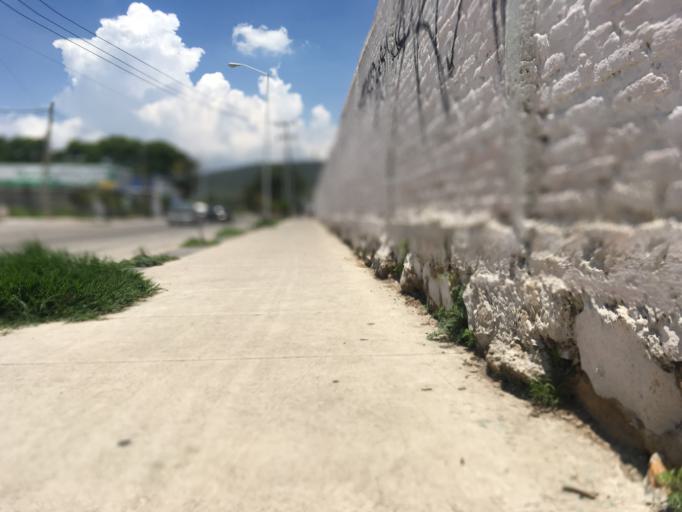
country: MX
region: Jalisco
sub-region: Tlajomulco de Zuniga
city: Jardines de San Sebastian
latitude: 20.5270
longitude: -103.4245
